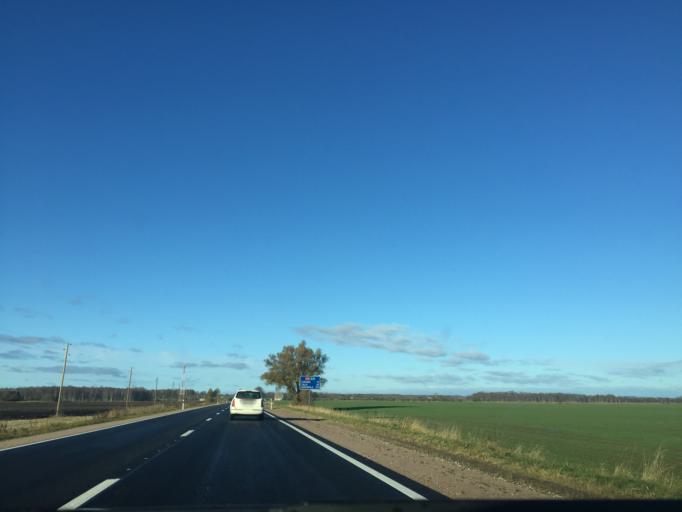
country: LV
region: Engure
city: Smarde
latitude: 56.9142
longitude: 23.3391
